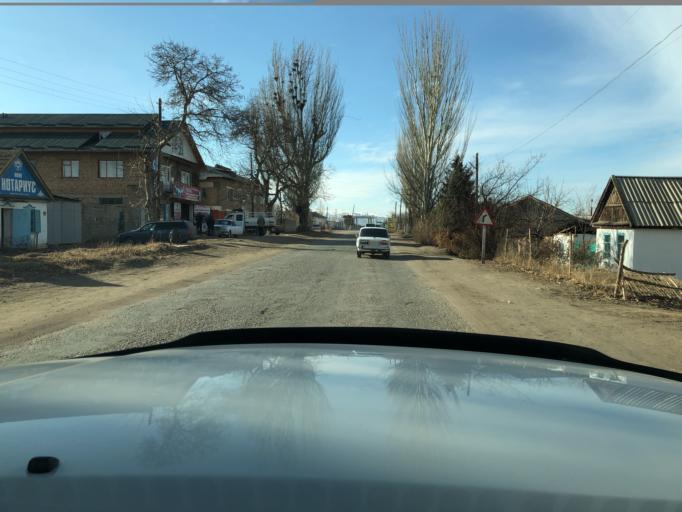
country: KG
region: Ysyk-Koel
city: Pokrovka
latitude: 42.3350
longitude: 77.9893
